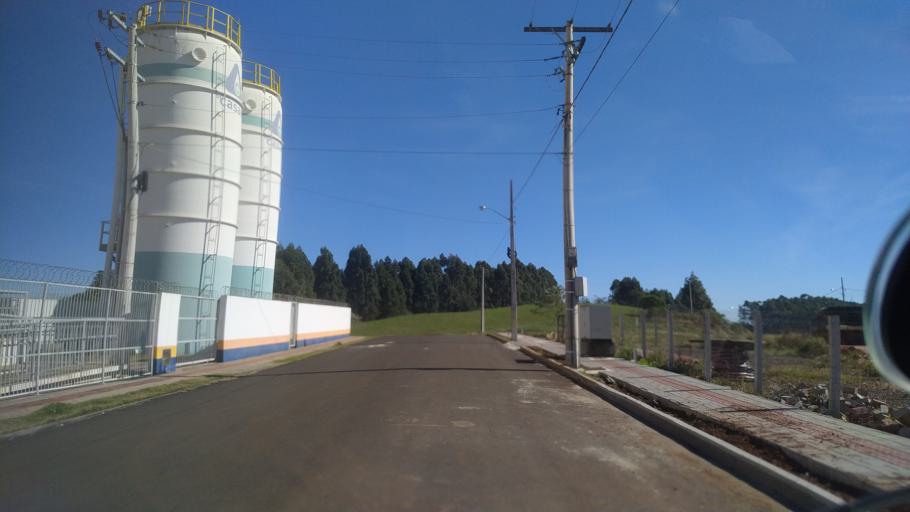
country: BR
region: Santa Catarina
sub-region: Chapeco
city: Chapeco
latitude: -27.0487
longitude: -52.6036
